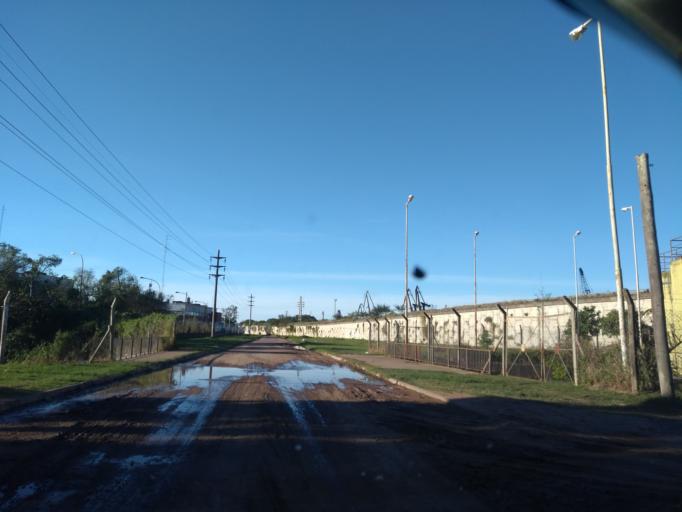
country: AR
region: Chaco
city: Barranqueras
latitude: -27.4937
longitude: -58.9289
